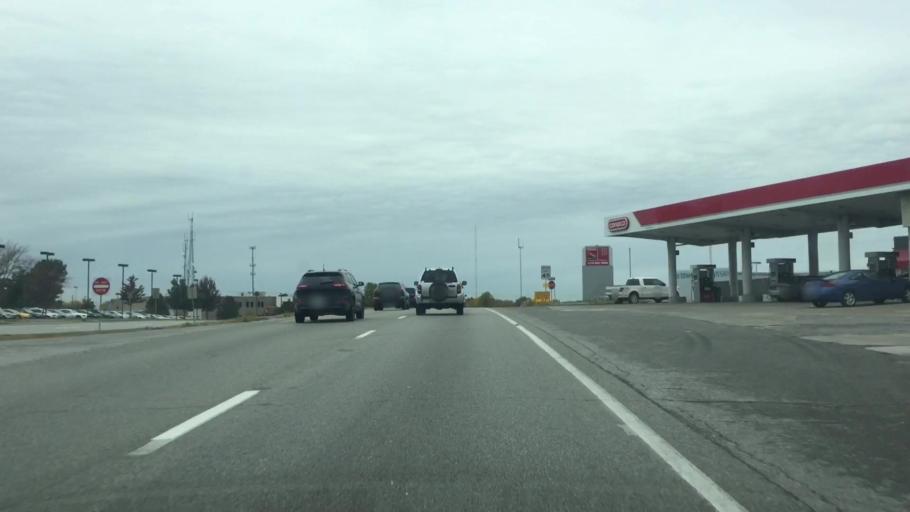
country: US
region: Missouri
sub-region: Jackson County
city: Raytown
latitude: 38.9981
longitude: -94.4789
